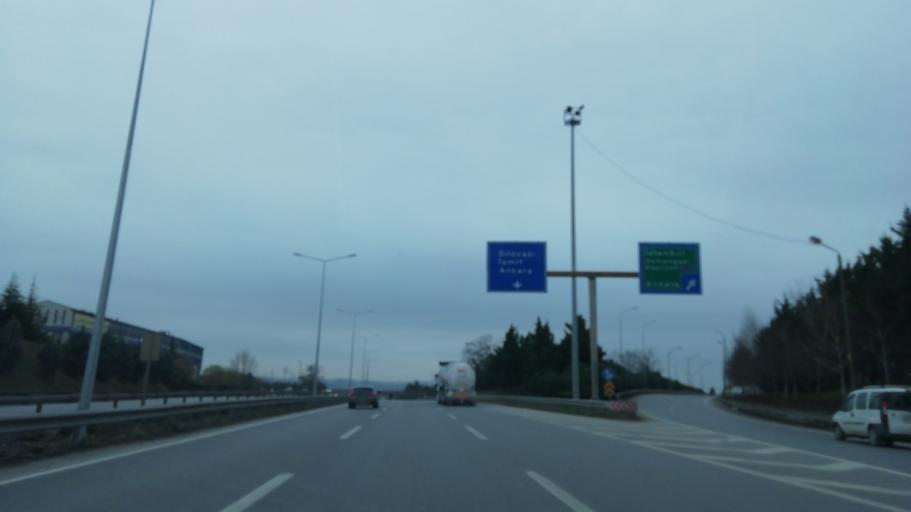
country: TR
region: Kocaeli
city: Gebze
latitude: 40.8014
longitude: 29.4692
